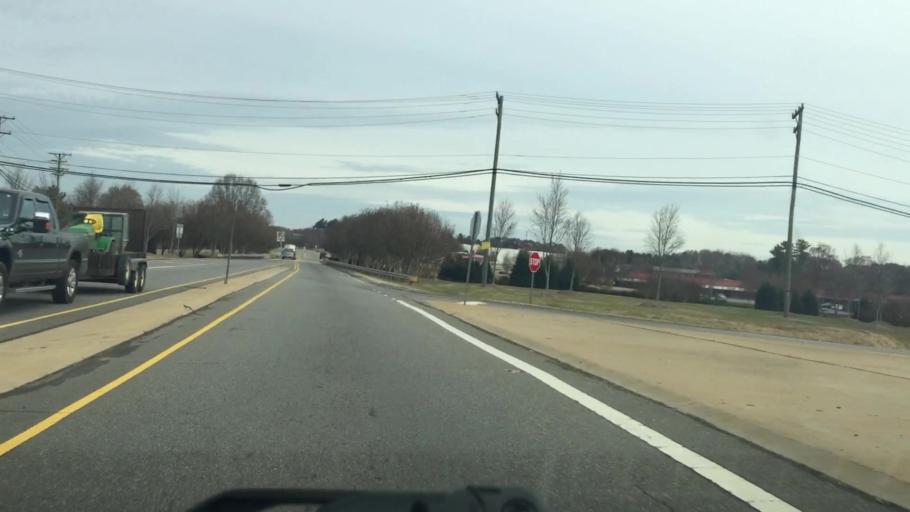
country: US
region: North Carolina
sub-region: Iredell County
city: Mooresville
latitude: 35.5877
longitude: -80.8380
